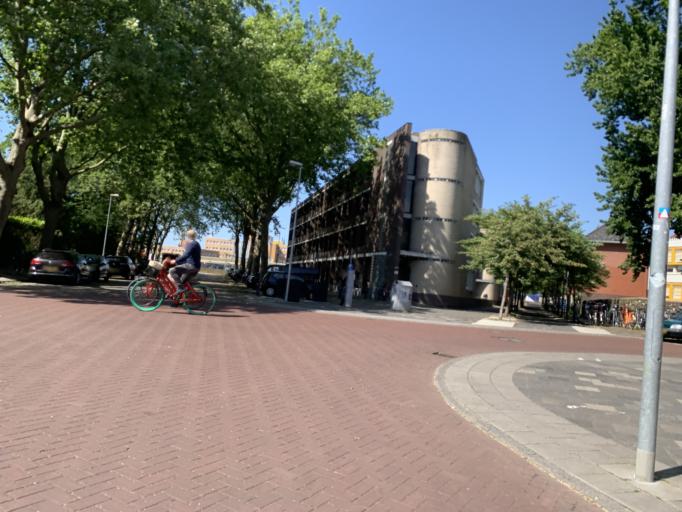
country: NL
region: Groningen
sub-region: Gemeente Groningen
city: Groningen
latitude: 53.2087
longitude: 6.5678
